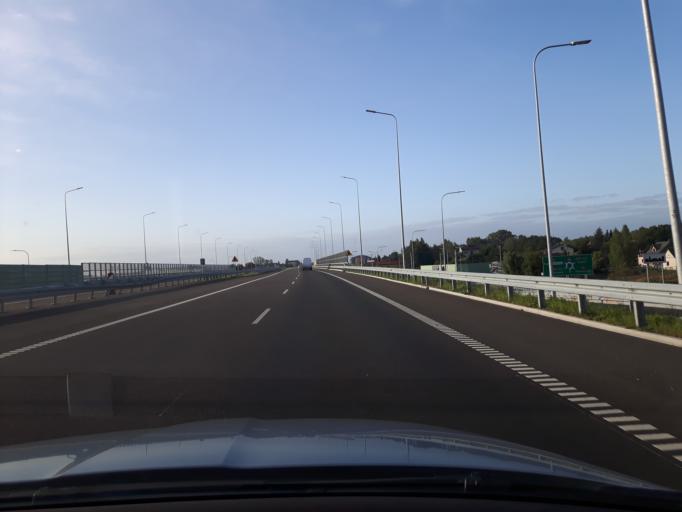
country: PL
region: Masovian Voivodeship
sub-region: Powiat radomski
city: Wolanow
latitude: 51.3905
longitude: 21.0211
